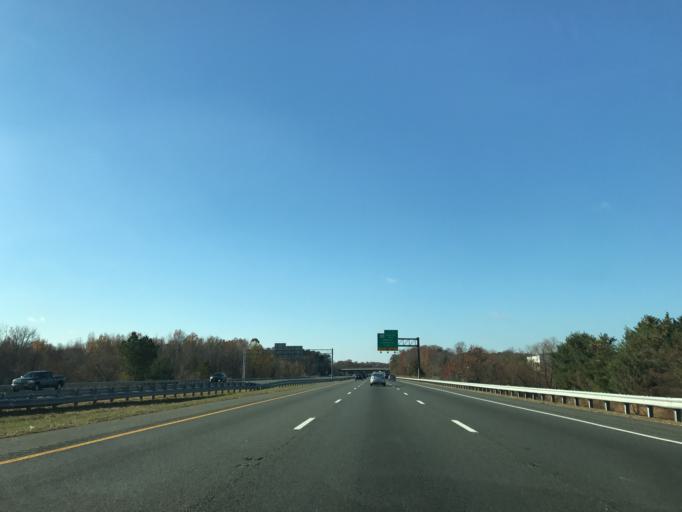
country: US
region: Maryland
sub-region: Anne Arundel County
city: Ferndale
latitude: 39.1568
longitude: -76.6608
